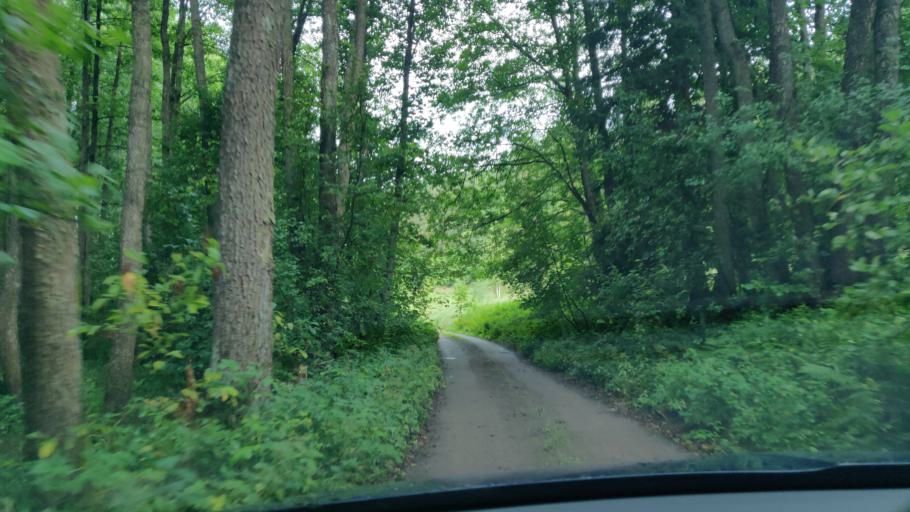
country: LT
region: Vilnius County
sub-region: Trakai
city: Rudiskes
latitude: 54.6074
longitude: 24.8421
